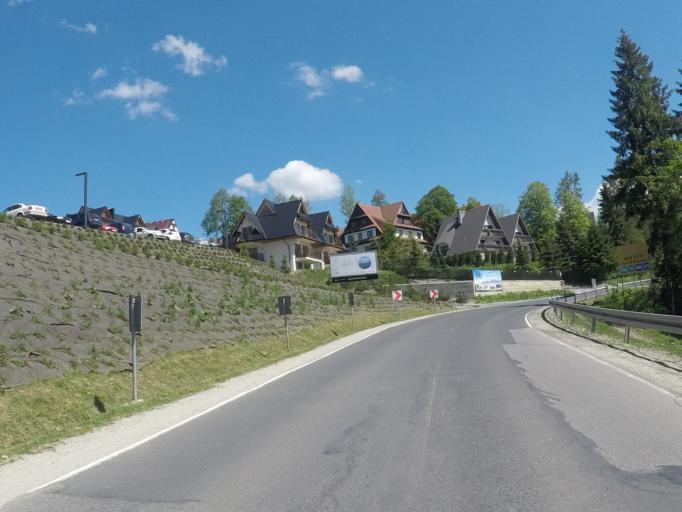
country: PL
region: Lesser Poland Voivodeship
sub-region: Powiat tatrzanski
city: Bukowina Tatrzanska
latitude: 49.3312
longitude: 20.0912
